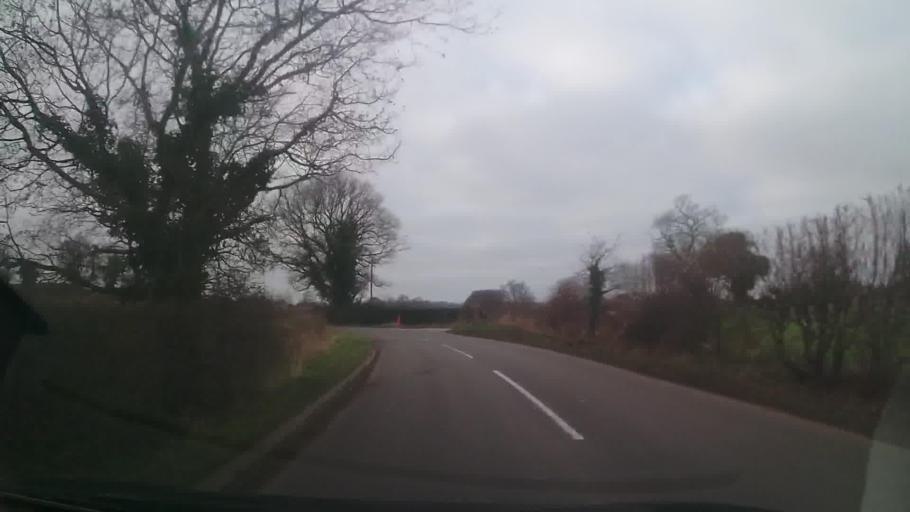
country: GB
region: England
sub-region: Shropshire
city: Petton
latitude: 52.8471
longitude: -2.8037
